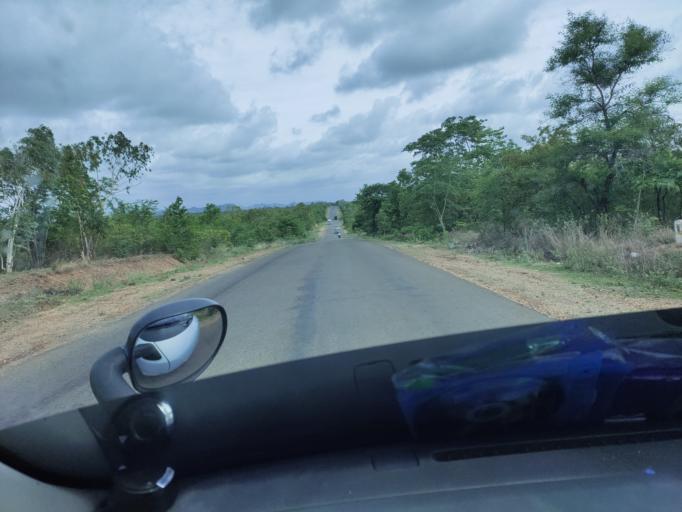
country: MM
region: Magway
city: Chauk
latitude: 20.9707
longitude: 95.0559
